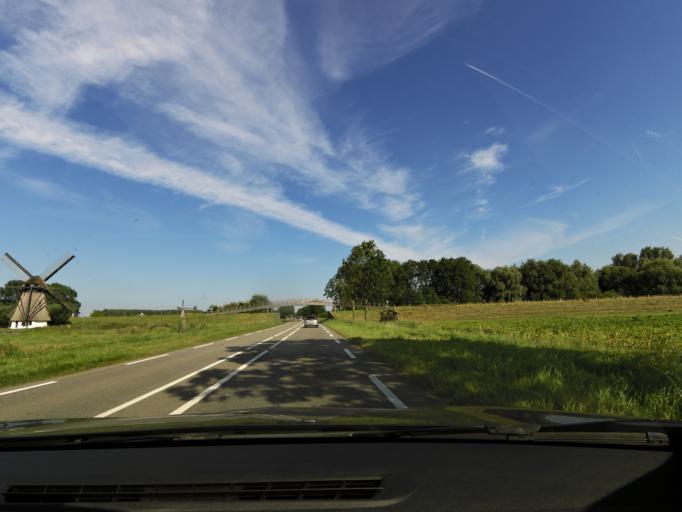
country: NL
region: North Brabant
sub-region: Gemeente Werkendam
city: Werkendam
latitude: 51.8006
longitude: 4.9151
